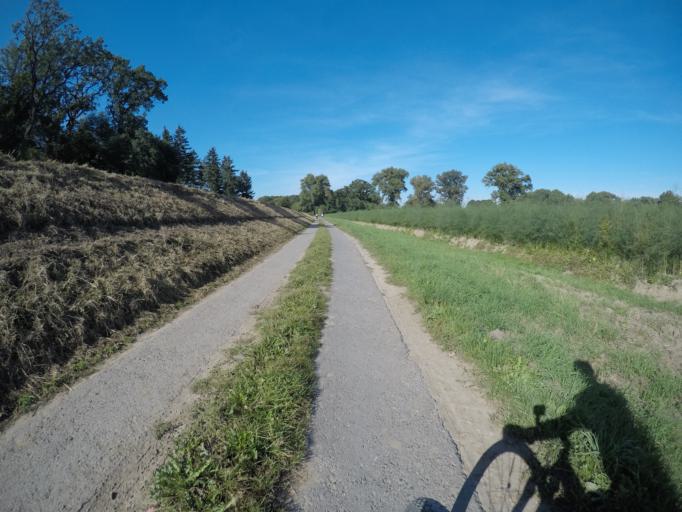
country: DE
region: Hesse
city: Griesheim
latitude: 49.8266
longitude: 8.5446
